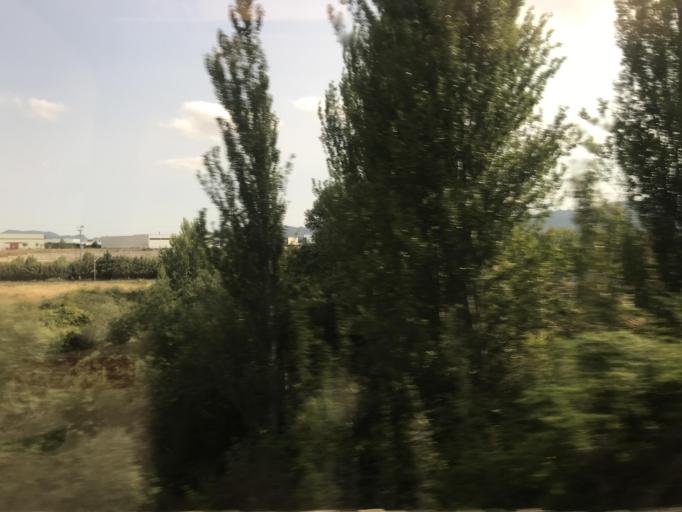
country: ES
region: Castille and Leon
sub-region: Provincia de Burgos
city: Miranda de Ebro
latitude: 42.6950
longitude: -2.9288
